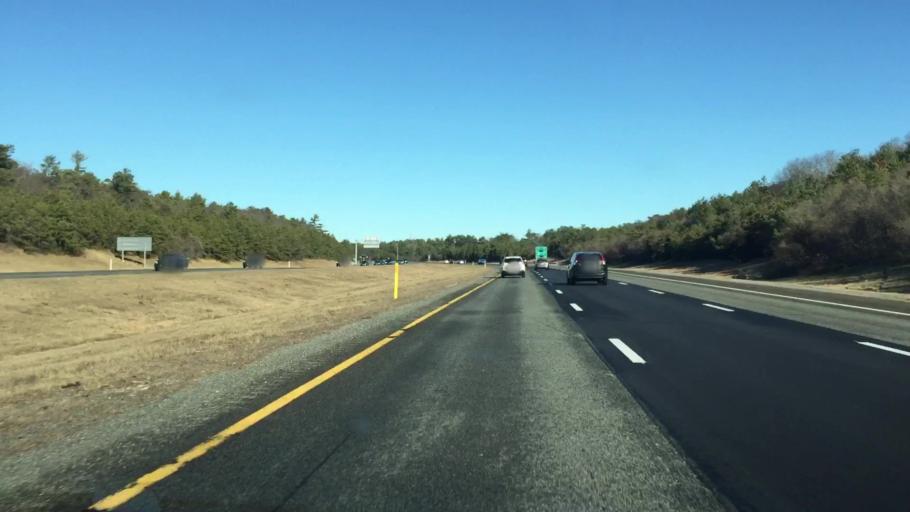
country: US
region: Massachusetts
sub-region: Barnstable County
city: Bourne
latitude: 41.7656
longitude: -70.5896
